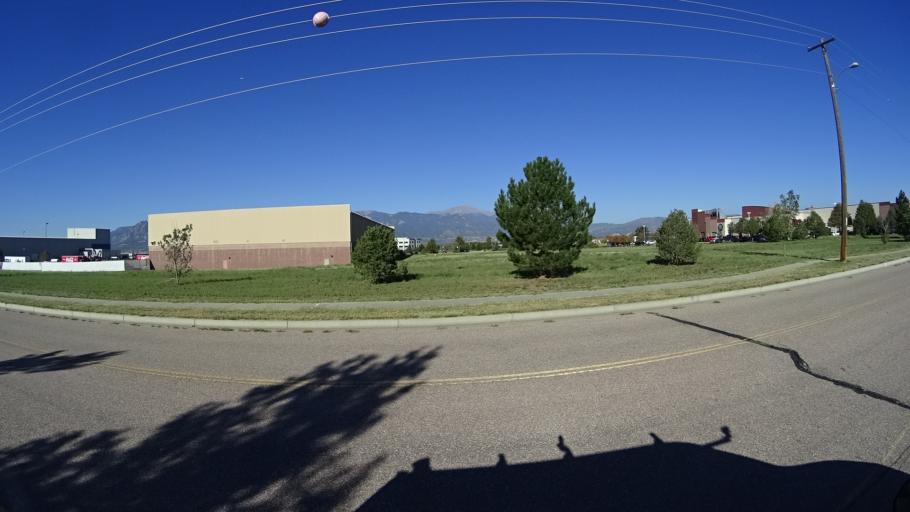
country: US
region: Colorado
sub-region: El Paso County
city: Cimarron Hills
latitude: 38.8178
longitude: -104.7225
